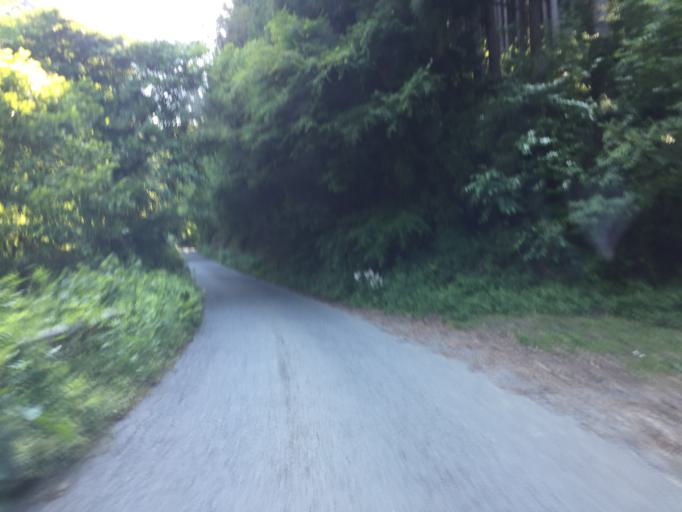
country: JP
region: Ibaraki
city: Kitaibaraki
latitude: 36.8691
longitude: 140.7013
